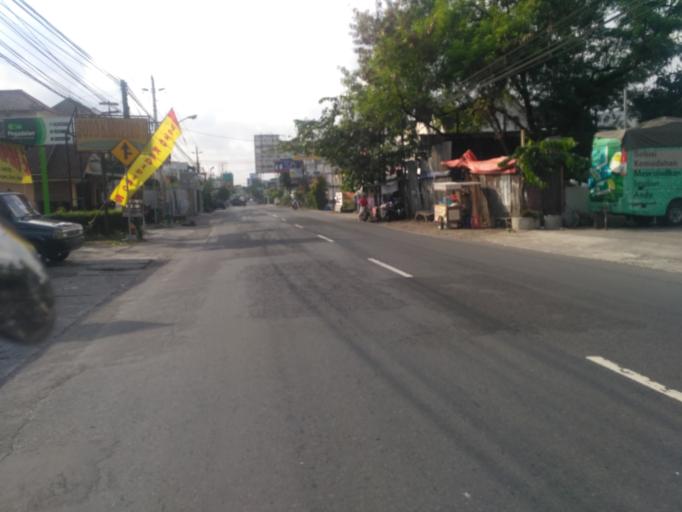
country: ID
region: Daerah Istimewa Yogyakarta
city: Gamping Lor
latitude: -7.7786
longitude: 110.3386
